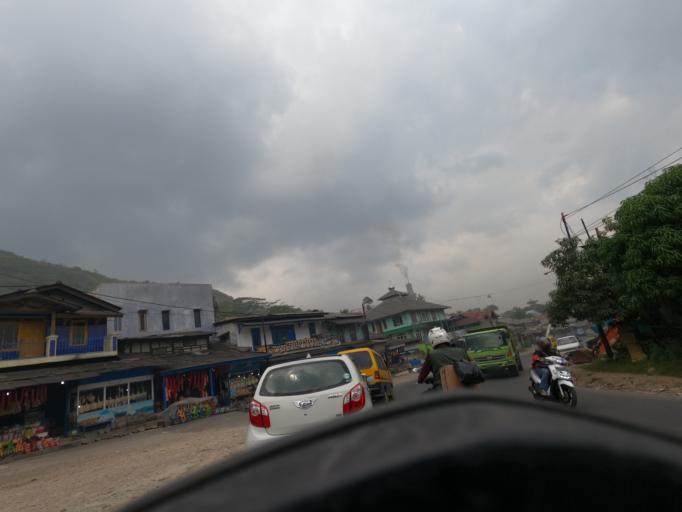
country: ID
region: West Java
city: Padalarang
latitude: -6.8317
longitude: 107.4520
